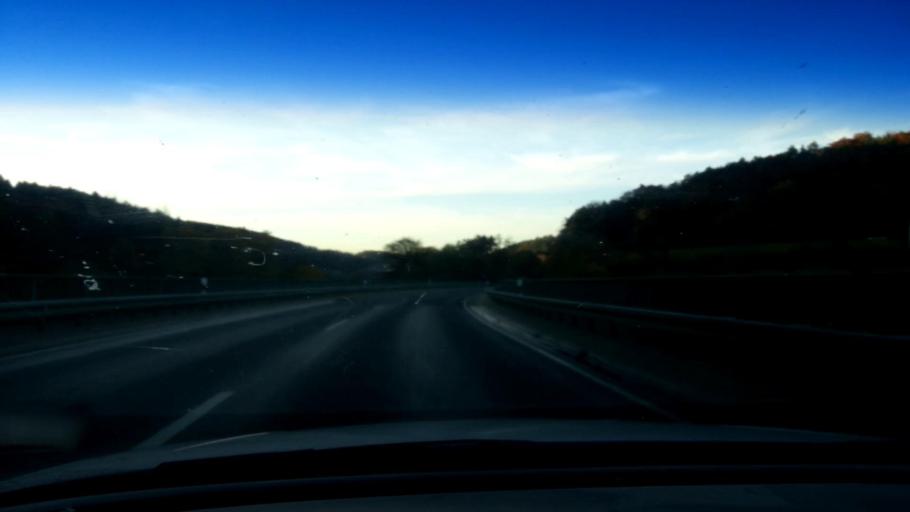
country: DE
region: Bavaria
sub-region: Upper Franconia
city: Unterleinleiter
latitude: 49.8441
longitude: 11.1923
